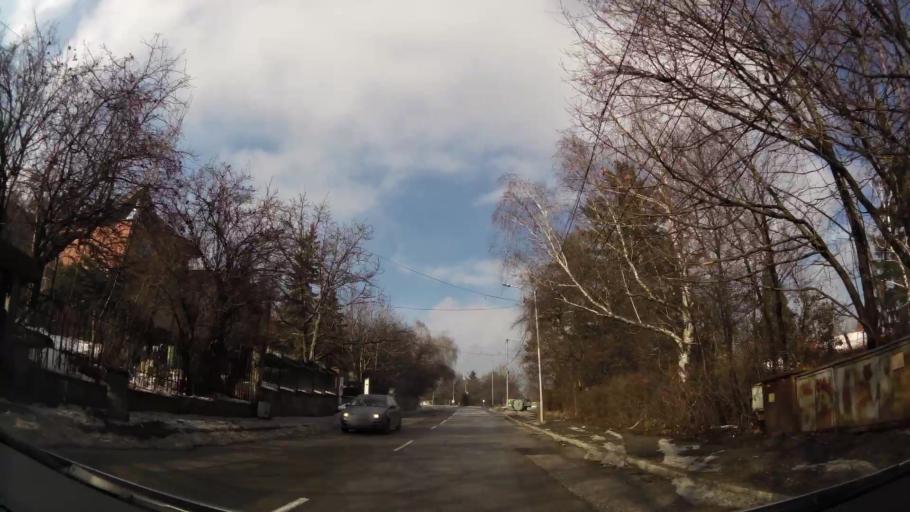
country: BG
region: Sofia-Capital
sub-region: Stolichna Obshtina
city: Sofia
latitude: 42.6496
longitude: 23.2500
